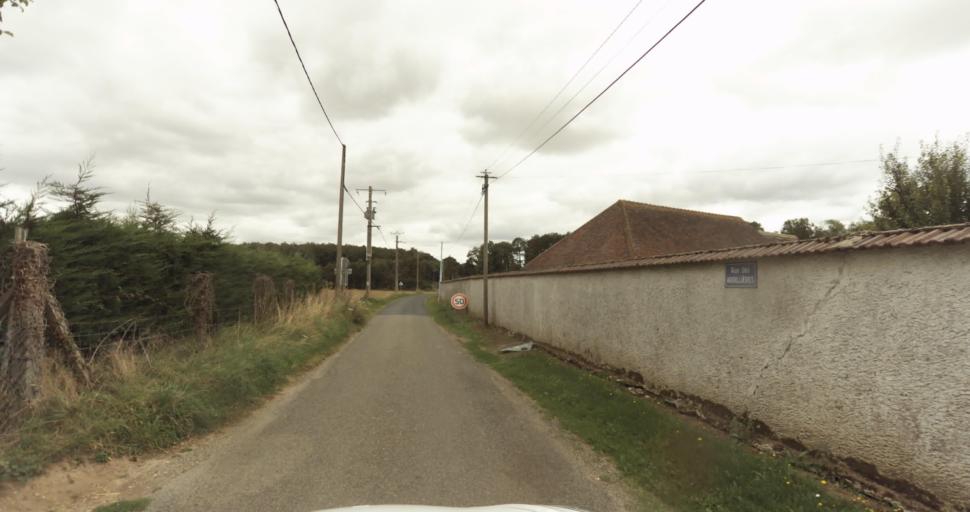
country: FR
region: Haute-Normandie
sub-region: Departement de l'Eure
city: Nonancourt
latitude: 48.8142
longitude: 1.1717
